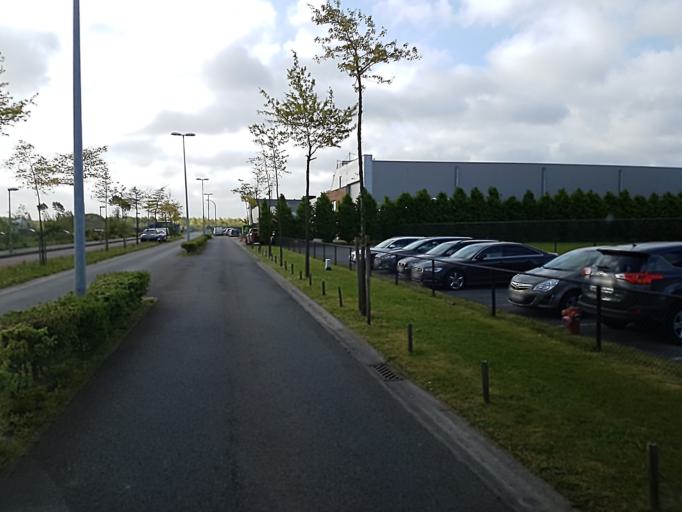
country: BE
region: Flanders
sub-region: Provincie Oost-Vlaanderen
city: Temse
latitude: 51.1212
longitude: 4.2030
